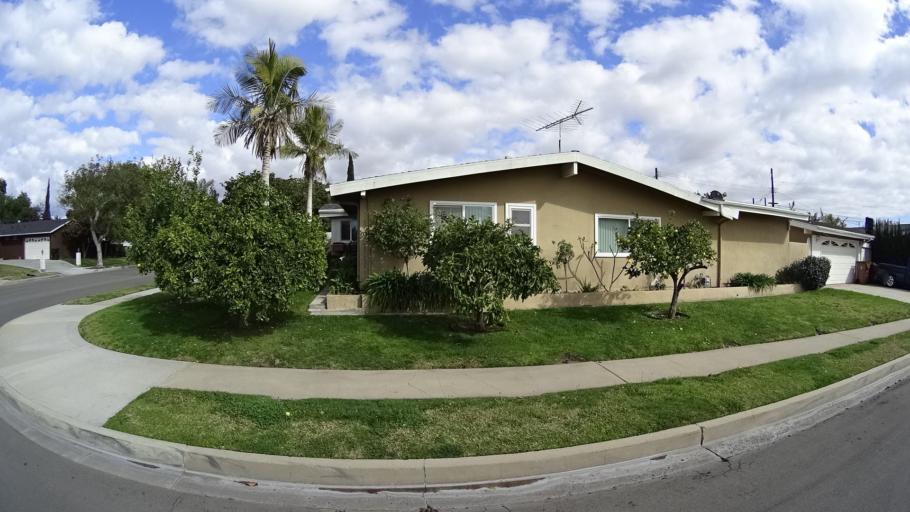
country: US
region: California
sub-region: Orange County
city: Anaheim
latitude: 33.8210
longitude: -117.9533
